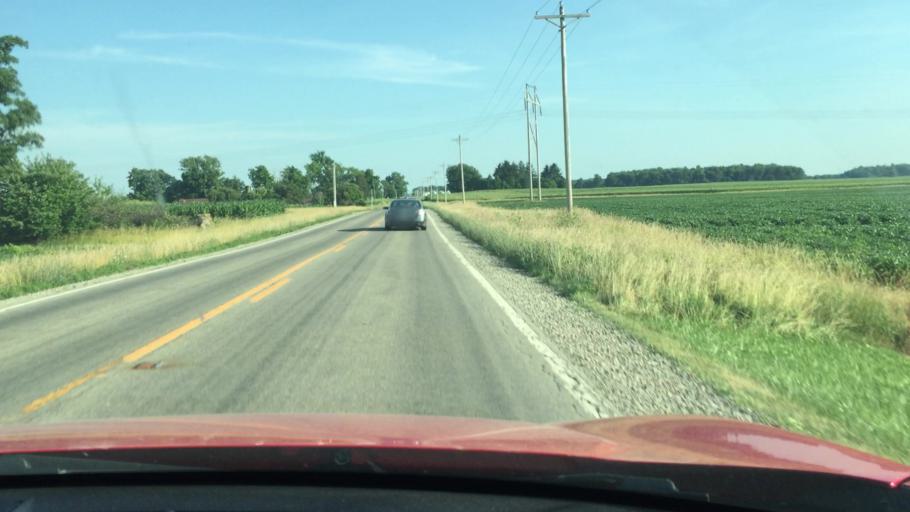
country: US
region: Ohio
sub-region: Hardin County
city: Ada
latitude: 40.6698
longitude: -83.8547
